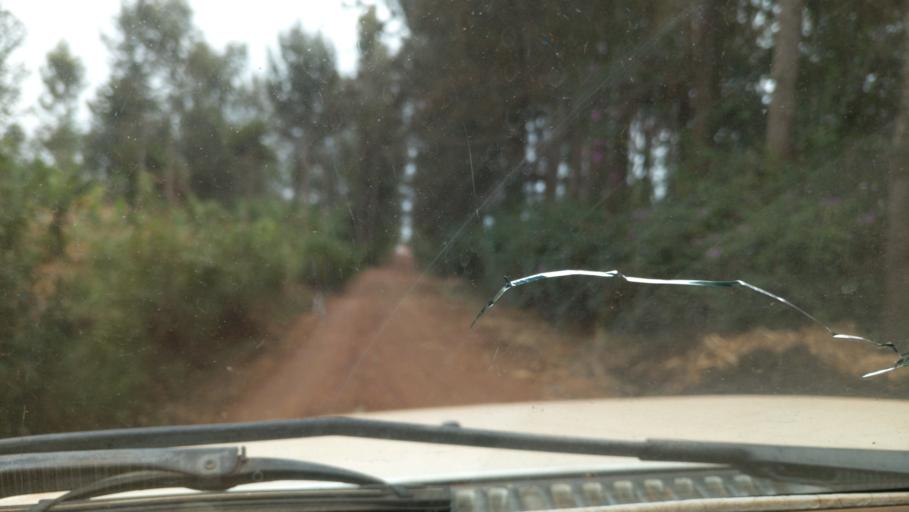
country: KE
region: Murang'a District
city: Maragua
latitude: -0.8895
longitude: 37.2135
